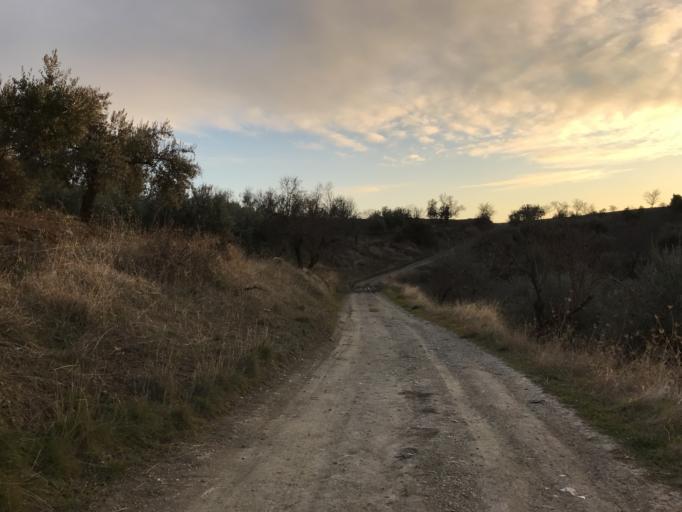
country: ES
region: Andalusia
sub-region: Provincia de Granada
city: Beas de Granada
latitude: 37.2121
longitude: -3.4847
